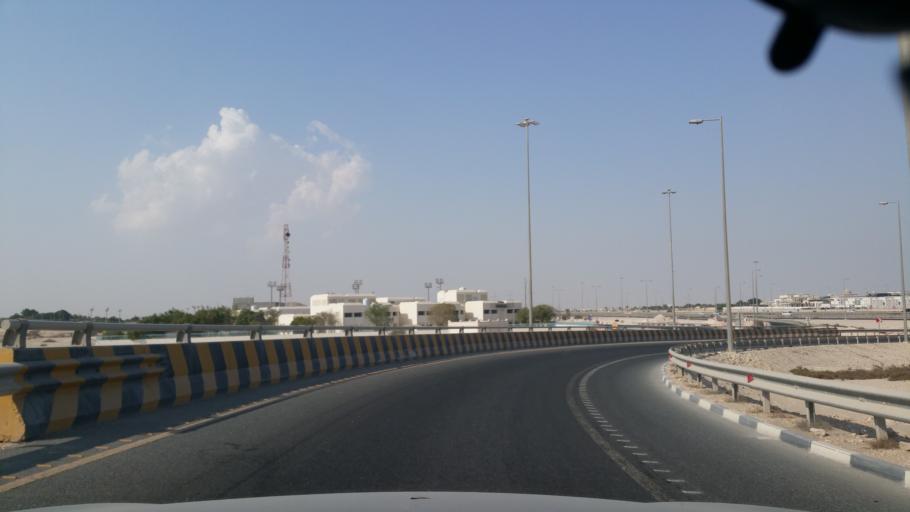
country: QA
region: Baladiyat Umm Salal
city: Umm Salal `Ali
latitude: 25.4489
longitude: 51.4079
